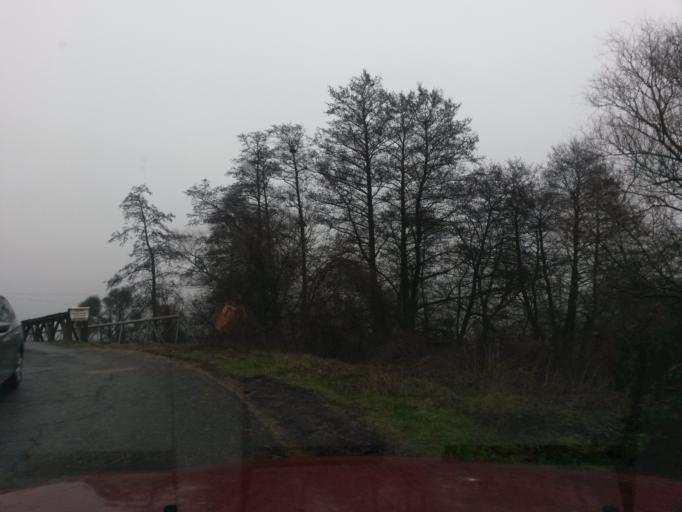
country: SK
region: Presovsky
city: Vranov nad Topl'ou
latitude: 48.8875
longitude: 21.7464
